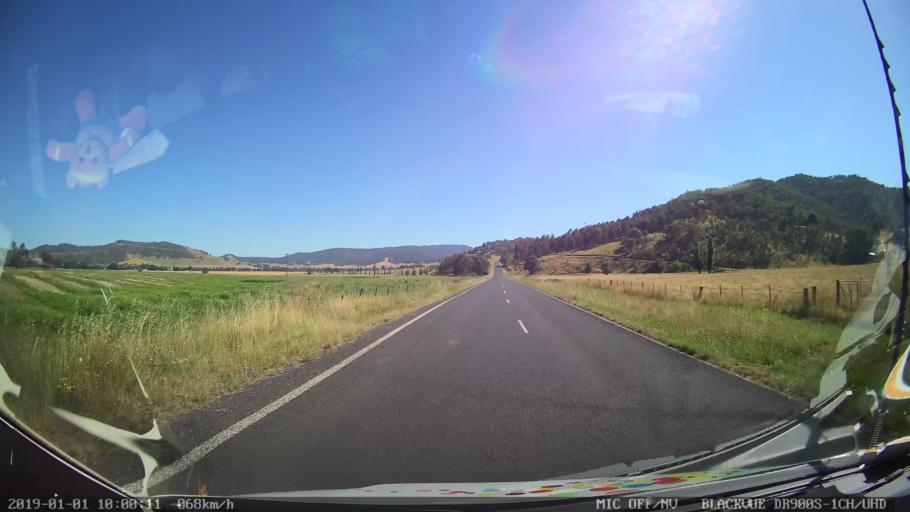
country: AU
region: New South Wales
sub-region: Snowy River
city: Jindabyne
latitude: -36.2047
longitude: 148.1022
